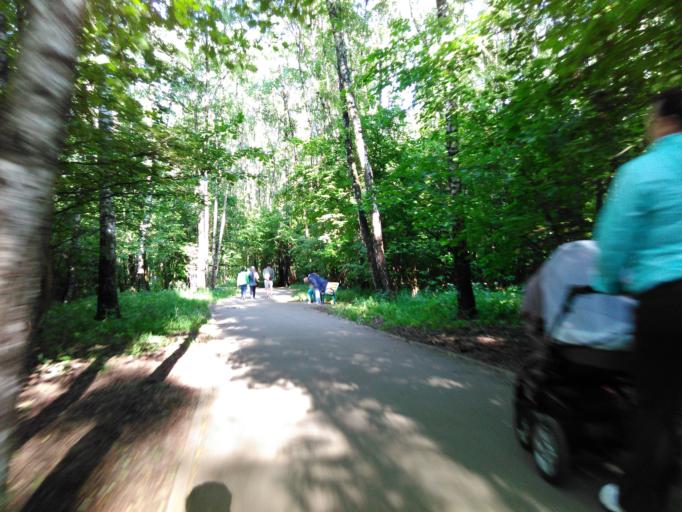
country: RU
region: Moscow
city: Troparevo
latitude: 55.6626
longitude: 37.4978
